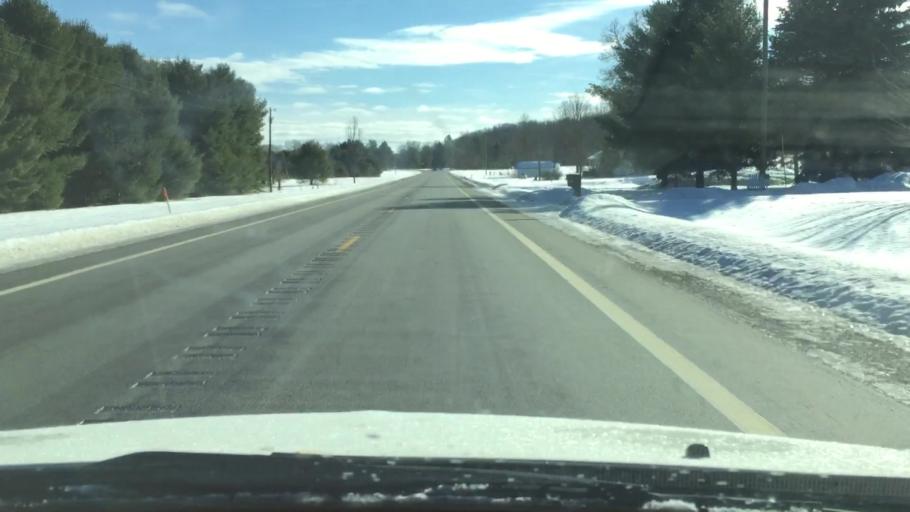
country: US
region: Michigan
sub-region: Charlevoix County
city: East Jordan
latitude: 45.0720
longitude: -85.0861
